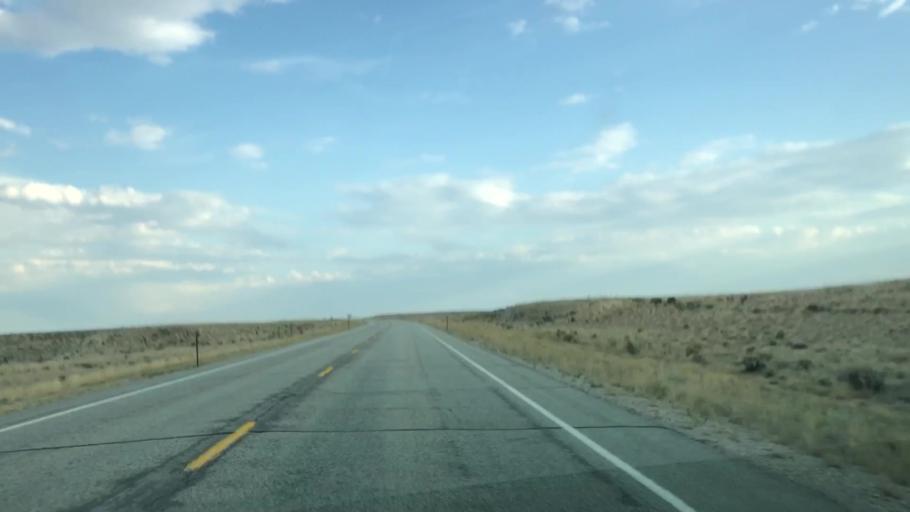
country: US
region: Wyoming
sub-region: Sweetwater County
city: North Rock Springs
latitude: 42.2828
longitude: -109.4867
